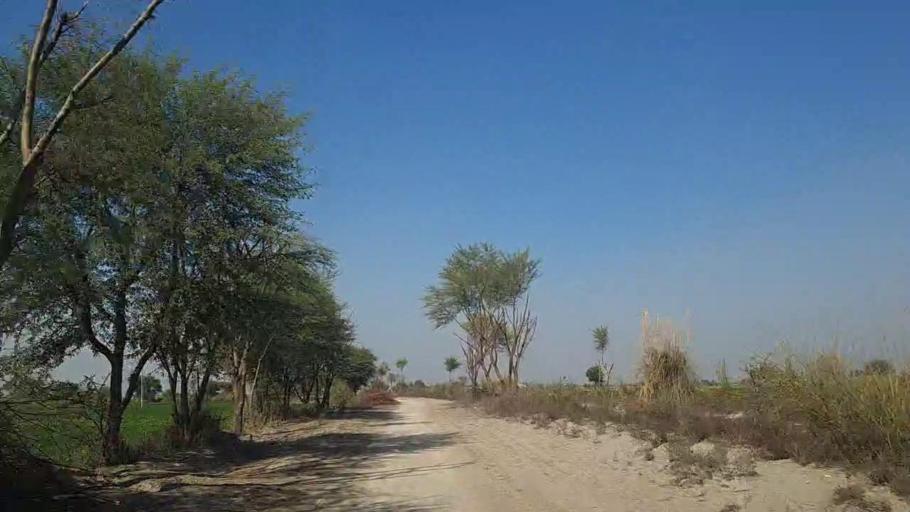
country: PK
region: Sindh
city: Sakrand
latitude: 26.2709
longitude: 68.2209
